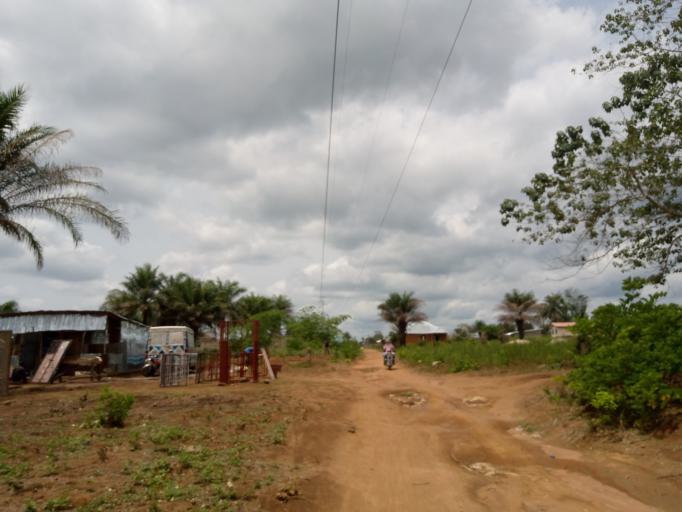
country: SL
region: Western Area
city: Waterloo
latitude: 8.3308
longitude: -13.0155
